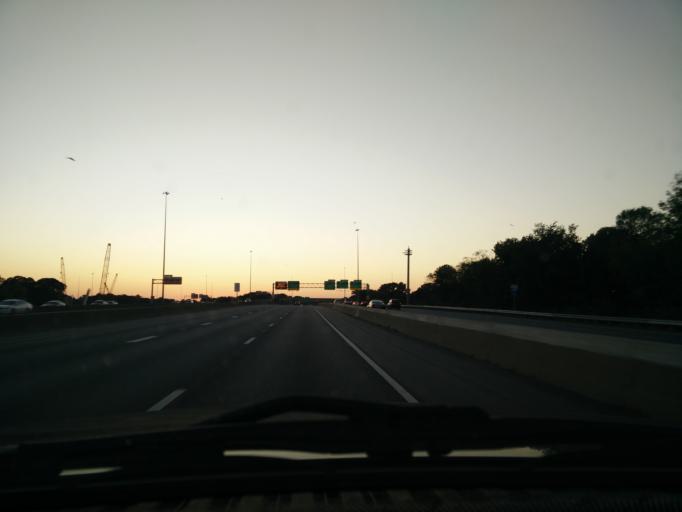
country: US
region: Virginia
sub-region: City of Chesapeake
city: Chesapeake
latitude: 36.8460
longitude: -76.1877
